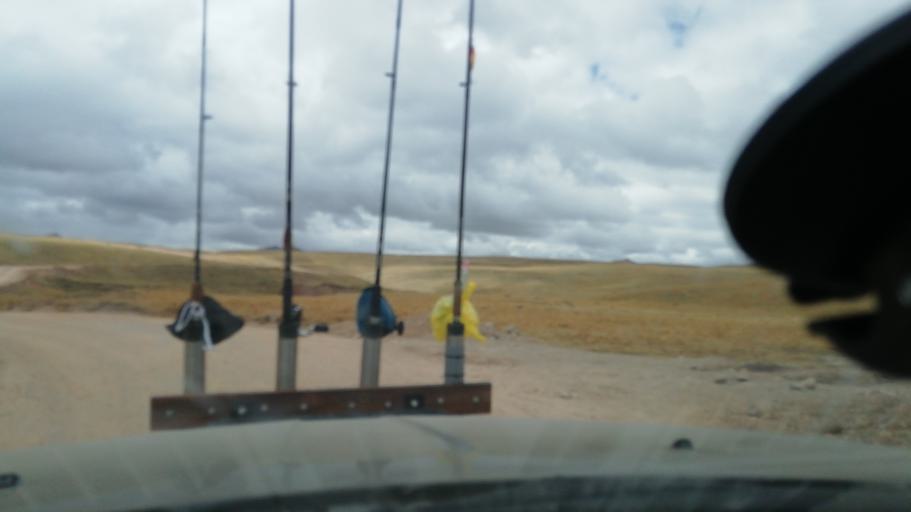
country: PE
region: Huancavelica
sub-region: Provincia de Huancavelica
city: Acobambilla
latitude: -12.5531
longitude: -75.5447
